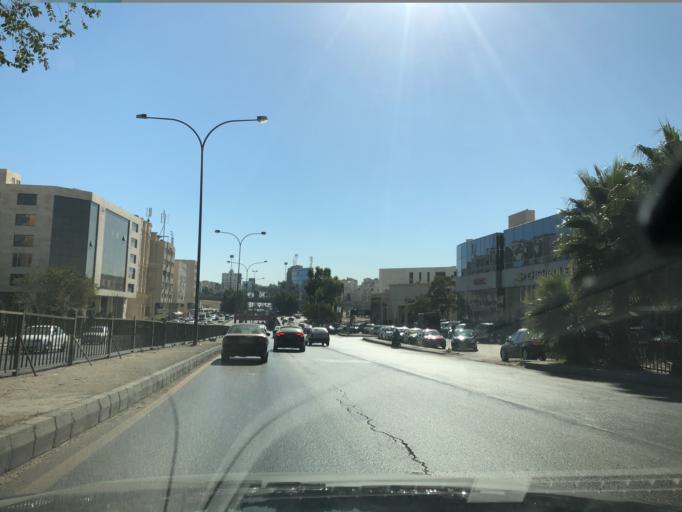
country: JO
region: Amman
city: Wadi as Sir
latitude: 31.9752
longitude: 35.8620
